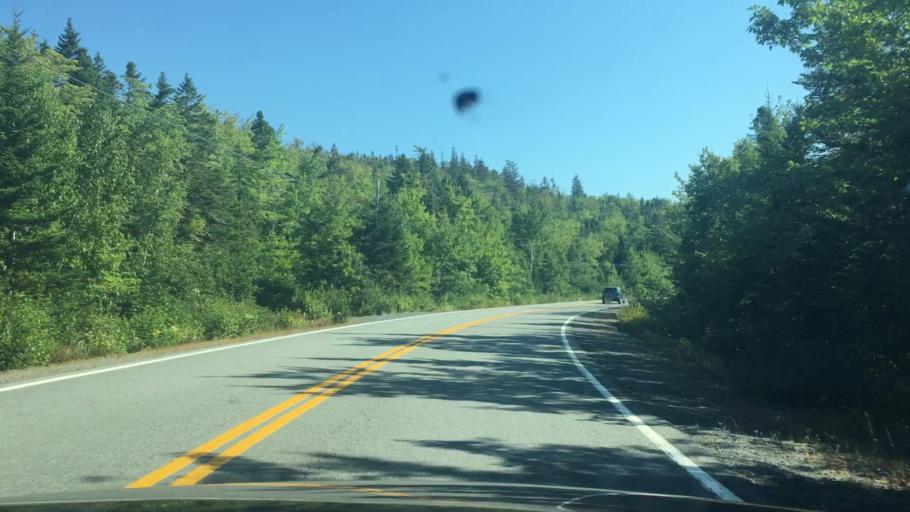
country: CA
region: Nova Scotia
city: Cole Harbour
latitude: 44.8161
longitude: -62.8841
